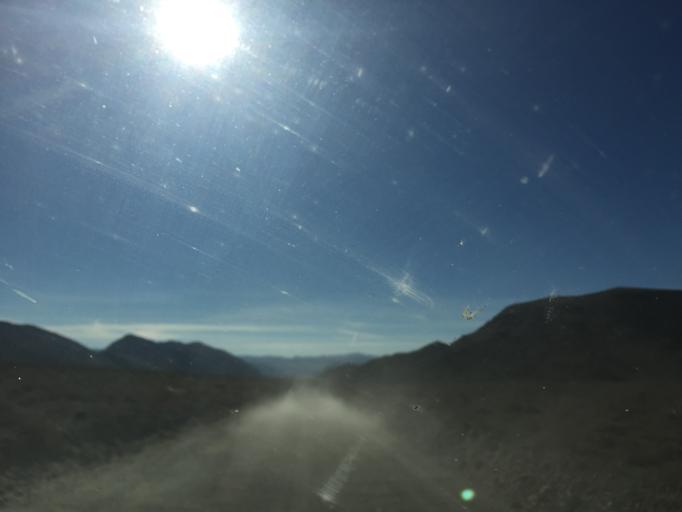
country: US
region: California
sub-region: Inyo County
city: Lone Pine
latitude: 36.8094
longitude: -117.5111
